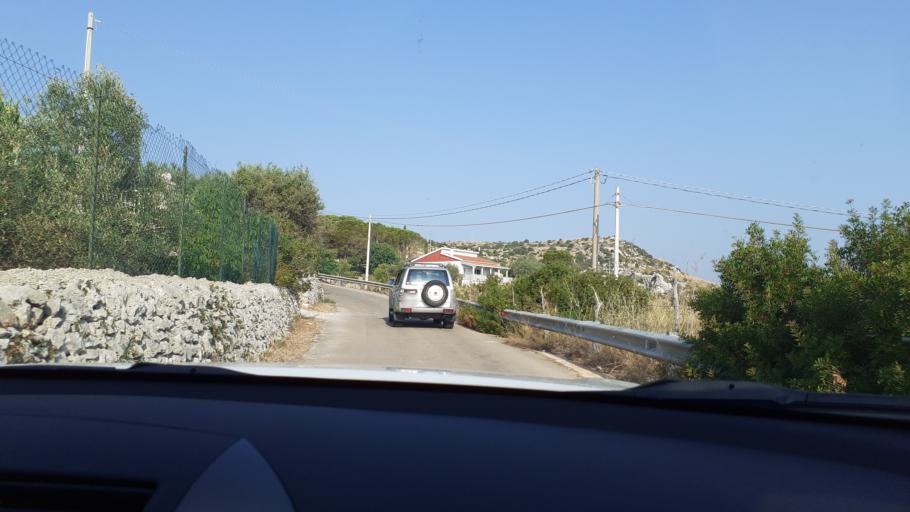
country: IT
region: Sicily
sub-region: Provincia di Siracusa
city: Cassibile
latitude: 36.9773
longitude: 15.1596
